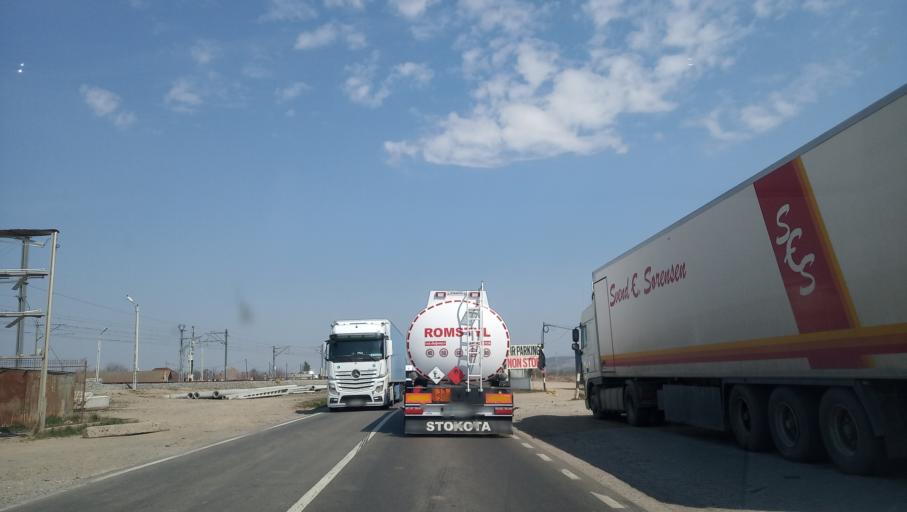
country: RO
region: Alba
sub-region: Municipiul Alba Iulia
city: Alba Iulia
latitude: 46.0595
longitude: 23.5826
